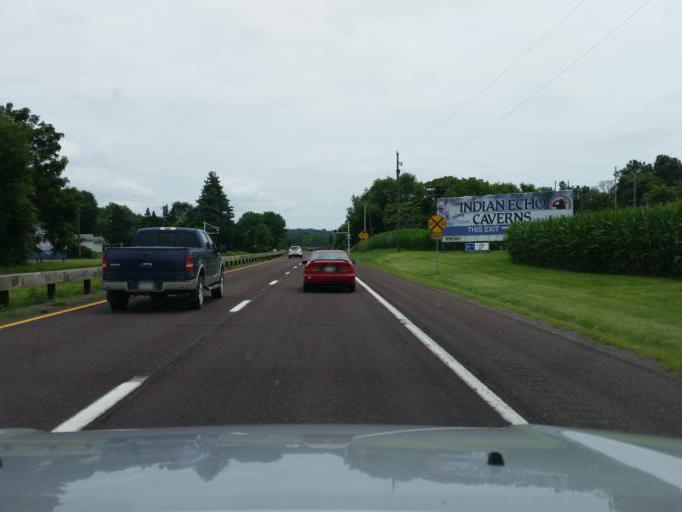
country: US
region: Pennsylvania
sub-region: Dauphin County
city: Hummelstown
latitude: 40.2596
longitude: -76.7176
